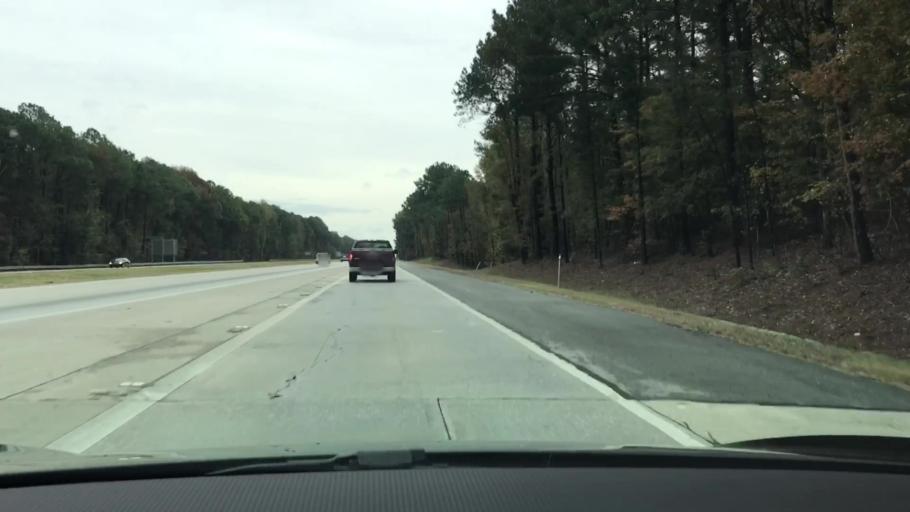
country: US
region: Georgia
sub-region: Greene County
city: Greensboro
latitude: 33.5459
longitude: -83.1999
